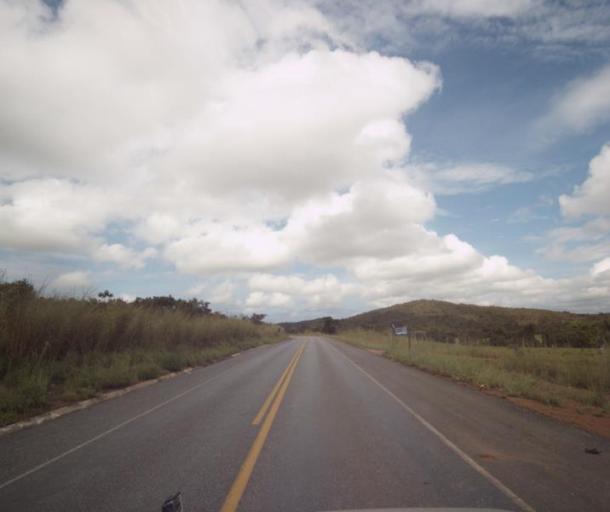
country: BR
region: Goias
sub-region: Pirenopolis
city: Pirenopolis
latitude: -15.6078
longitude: -48.6521
